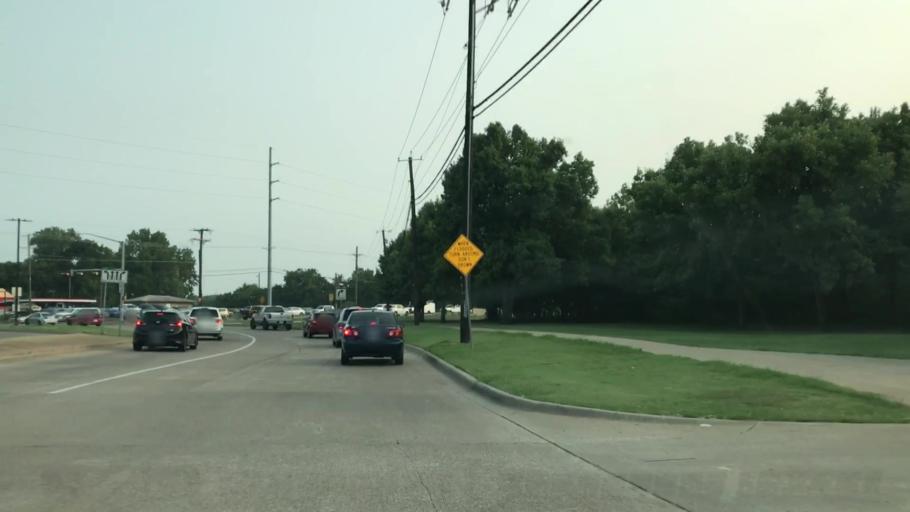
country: US
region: Texas
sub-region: Dallas County
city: Garland
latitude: 32.8722
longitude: -96.6311
